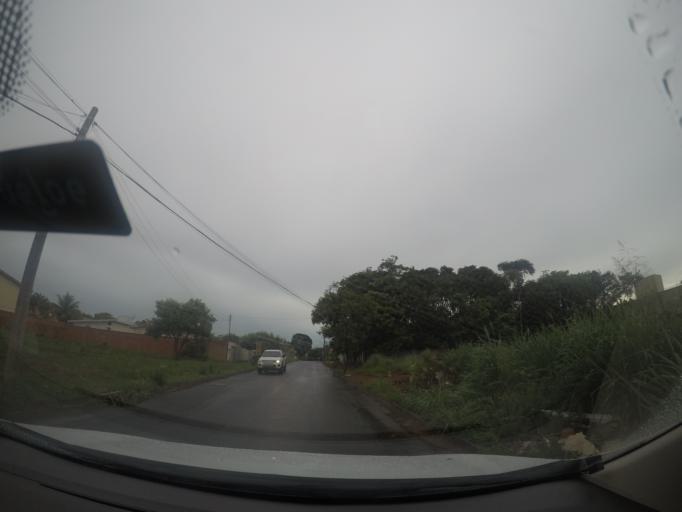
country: BR
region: Goias
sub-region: Goiania
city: Goiania
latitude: -16.6357
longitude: -49.2294
